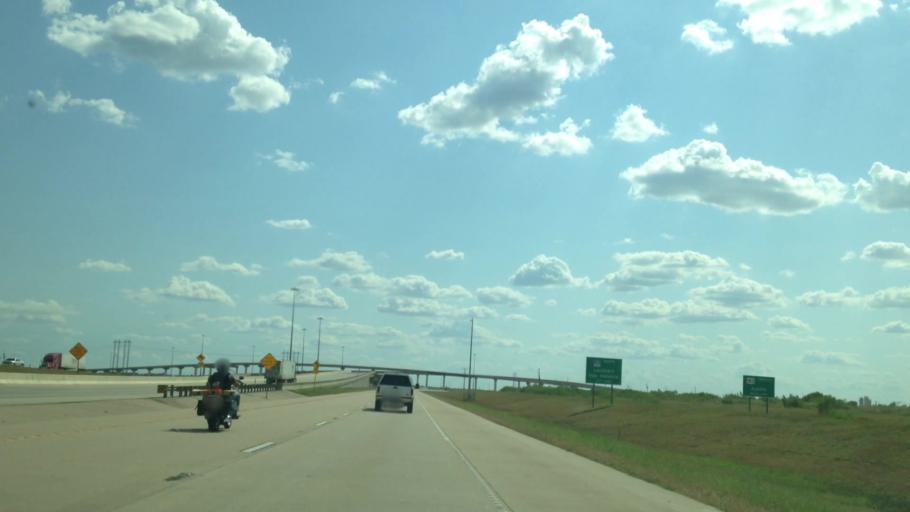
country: US
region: Texas
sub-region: Travis County
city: Onion Creek
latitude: 30.0892
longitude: -97.6852
